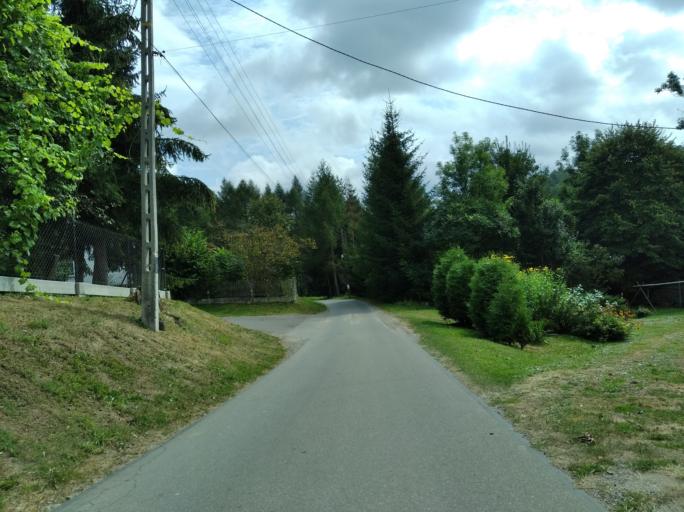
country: PL
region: Subcarpathian Voivodeship
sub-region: Powiat krosnienski
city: Wojaszowka
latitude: 49.7868
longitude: 21.6957
